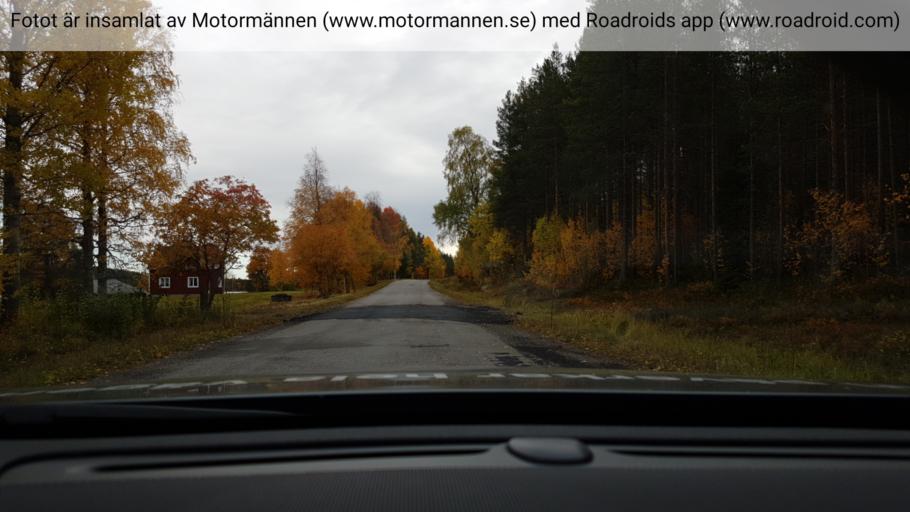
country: SE
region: Norrbotten
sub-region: Overkalix Kommun
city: OEverkalix
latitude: 66.2386
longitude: 23.0068
